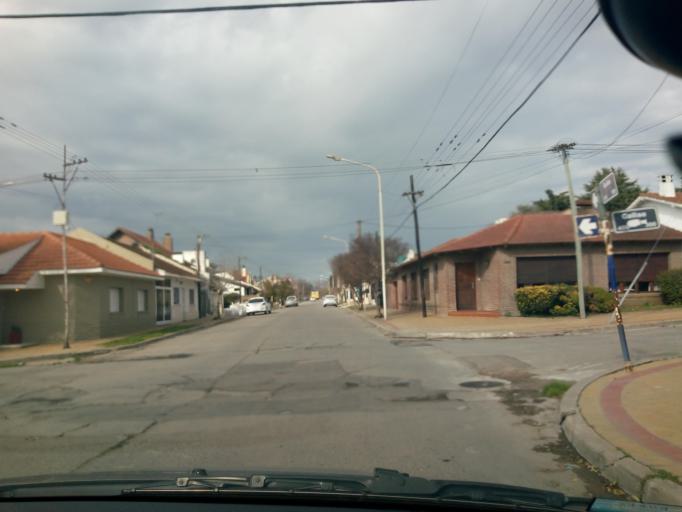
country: AR
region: Buenos Aires
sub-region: Partido de Tandil
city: Tandil
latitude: -37.3369
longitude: -59.1335
